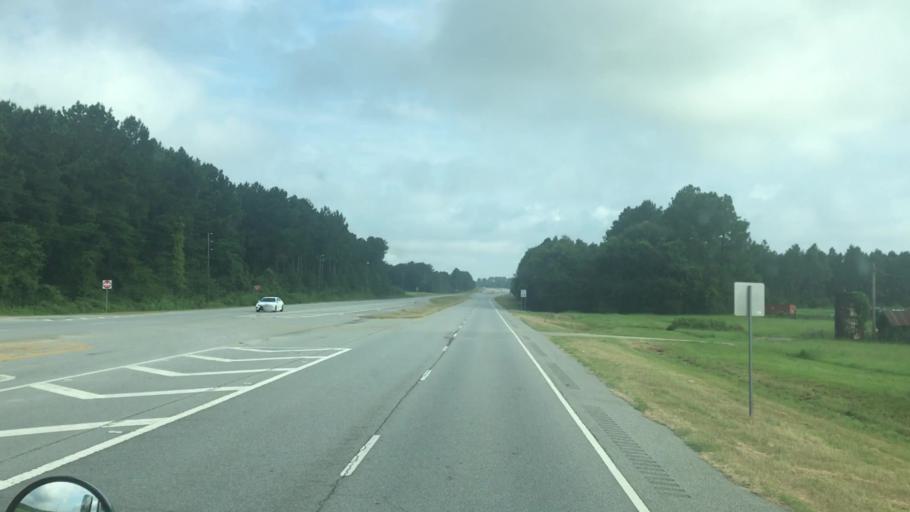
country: US
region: Georgia
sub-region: Miller County
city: Colquitt
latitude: 31.1962
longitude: -84.7675
